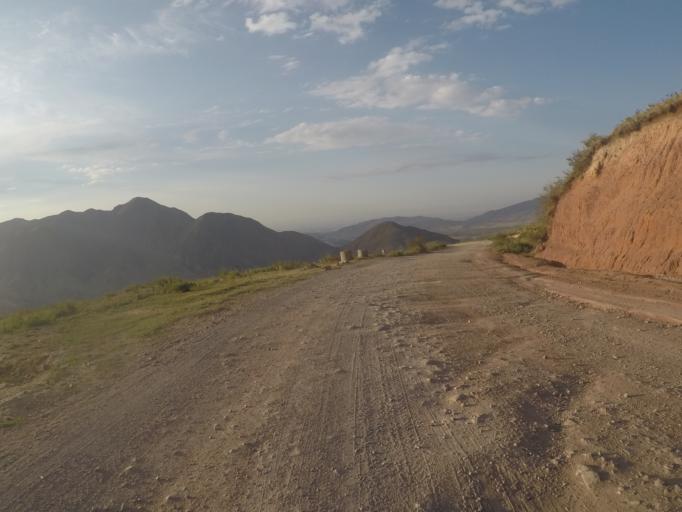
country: KG
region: Chuy
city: Bishkek
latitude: 42.6557
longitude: 74.6627
